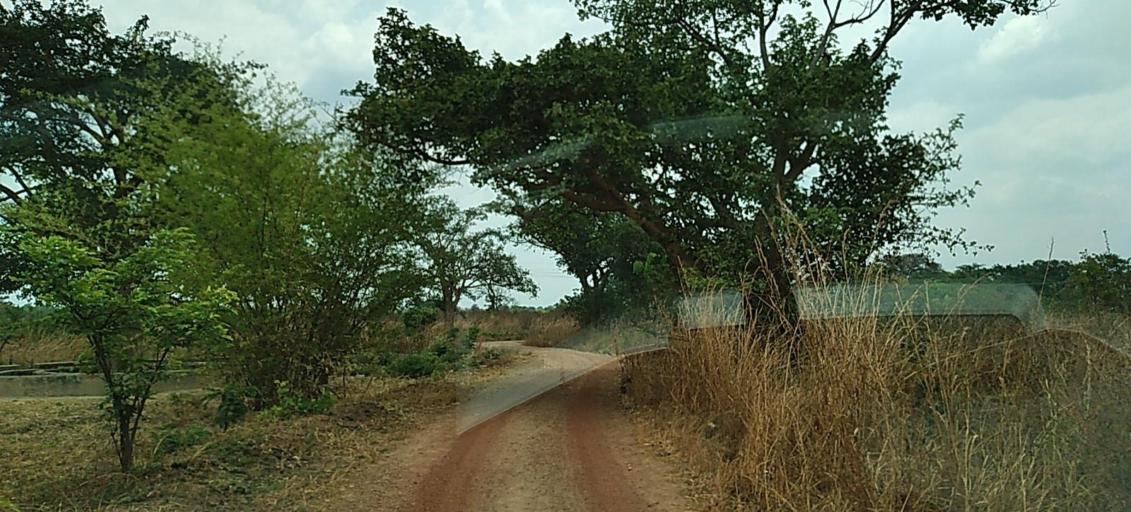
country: ZM
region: Copperbelt
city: Chililabombwe
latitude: -12.3132
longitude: 27.7905
